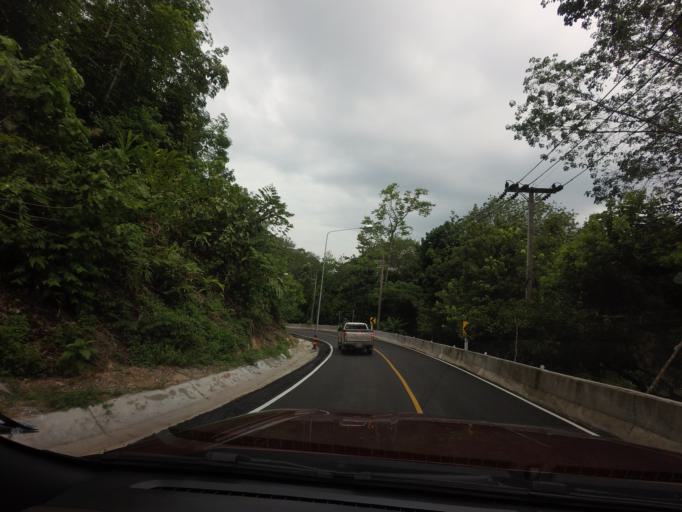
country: TH
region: Yala
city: Than To
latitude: 6.1373
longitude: 101.2967
